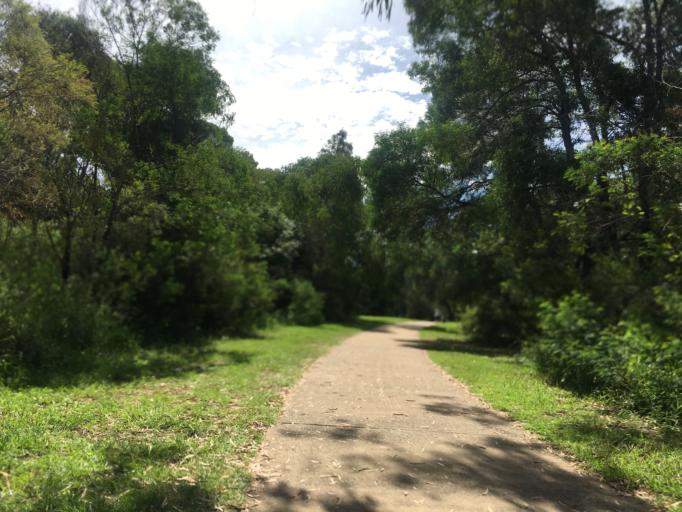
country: AU
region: New South Wales
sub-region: Camden
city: Camden South
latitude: -34.0680
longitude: 150.6990
